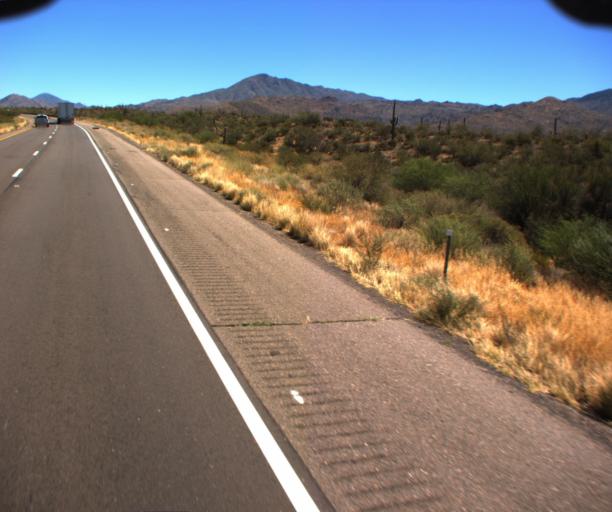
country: US
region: Arizona
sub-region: Maricopa County
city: Rio Verde
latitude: 33.7366
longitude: -111.5053
